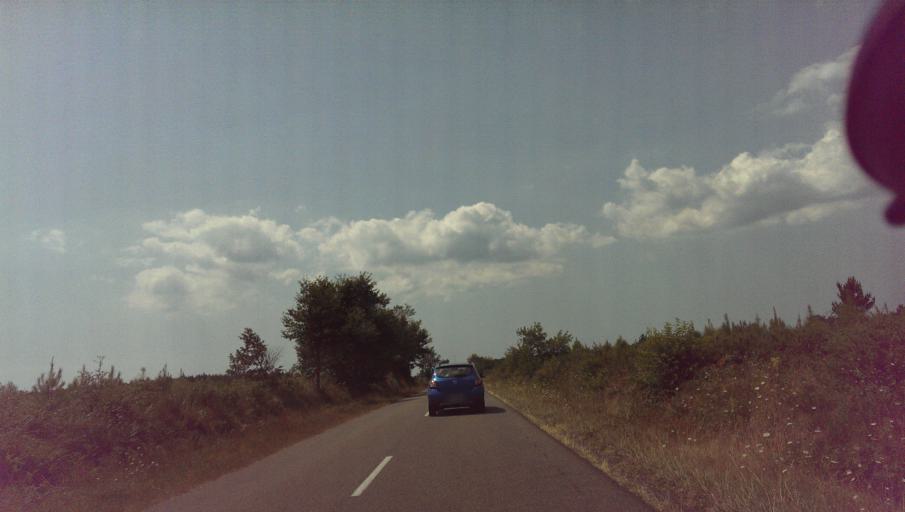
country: FR
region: Aquitaine
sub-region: Departement des Landes
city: Sabres
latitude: 44.1144
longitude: -0.6104
